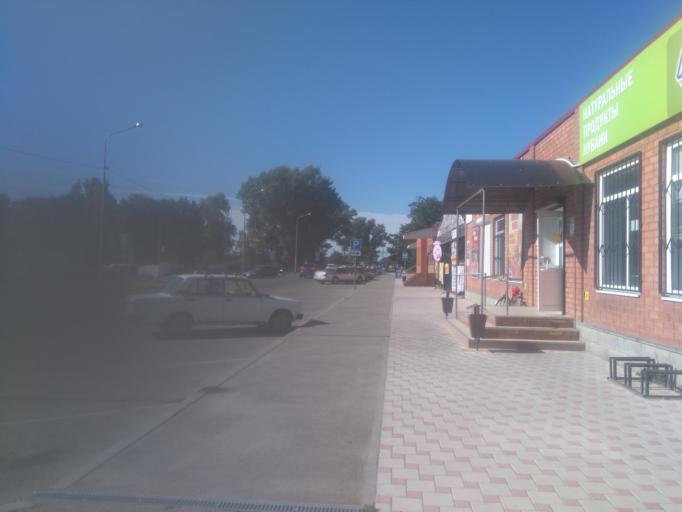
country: RU
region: Krasnodarskiy
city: Fastovetskaya
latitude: 45.9109
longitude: 40.1519
